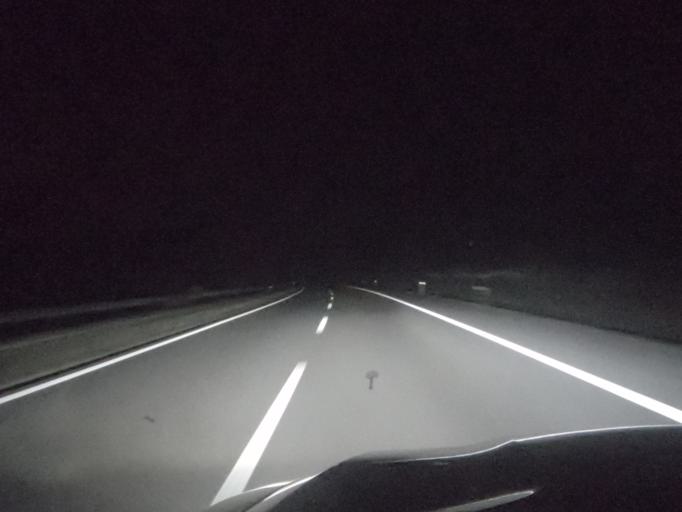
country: PT
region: Aveiro
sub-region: Aveiro
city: Eixo
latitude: 40.6026
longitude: -8.5528
